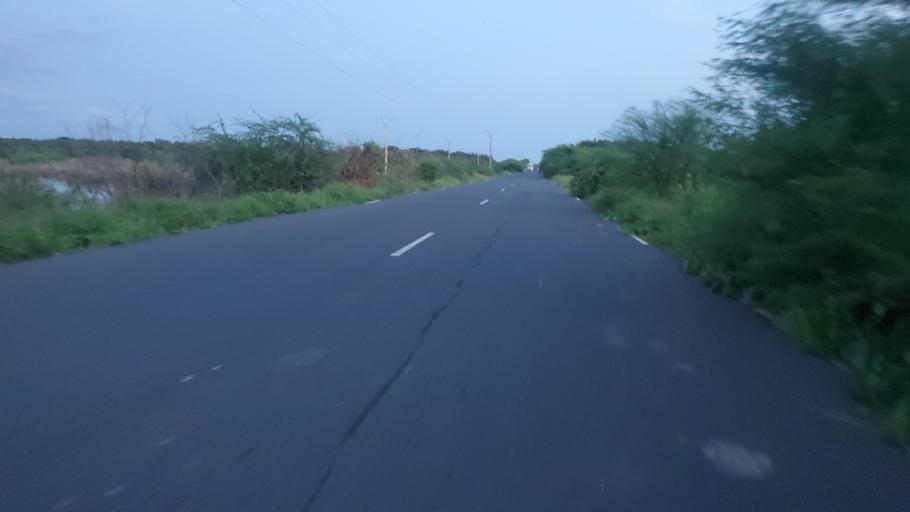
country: SN
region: Saint-Louis
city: Saint-Louis
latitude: 16.0812
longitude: -16.3921
